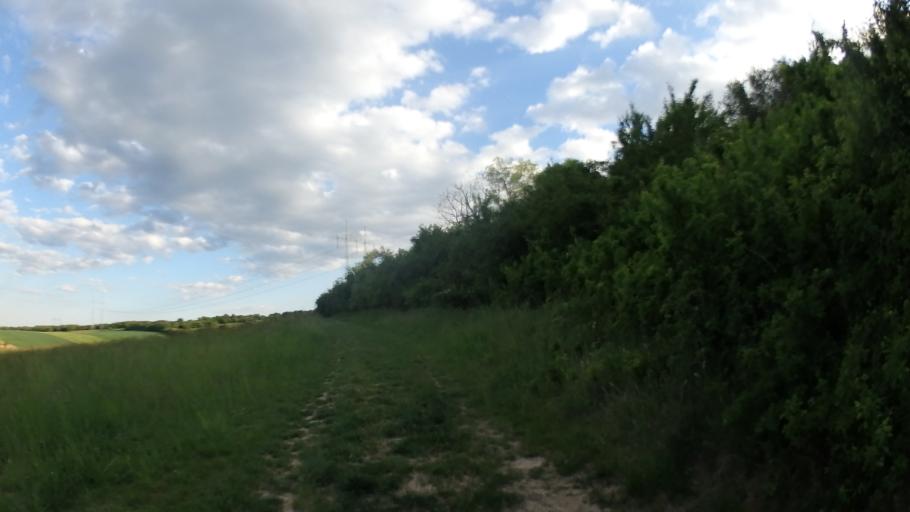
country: CZ
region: South Moravian
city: Zelesice
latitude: 49.1300
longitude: 16.5895
